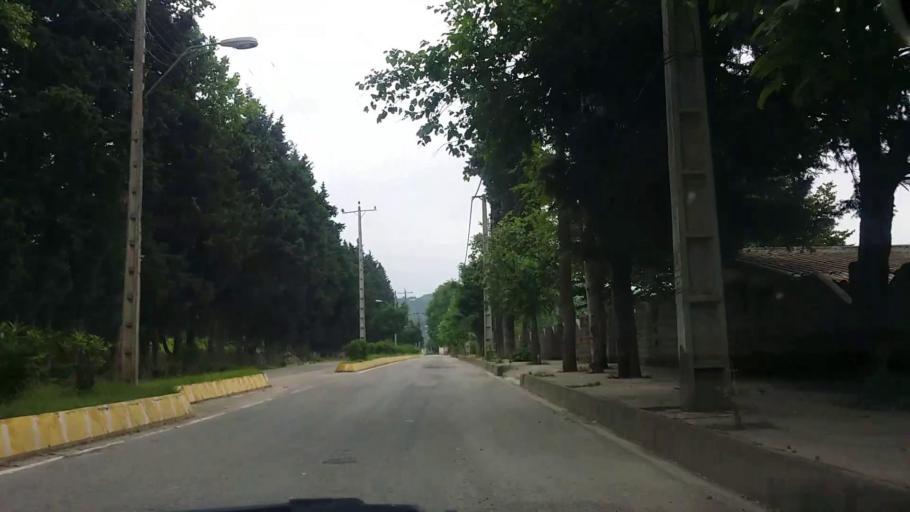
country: IR
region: Mazandaran
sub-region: Nowshahr
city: Nowshahr
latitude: 36.6316
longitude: 51.5026
